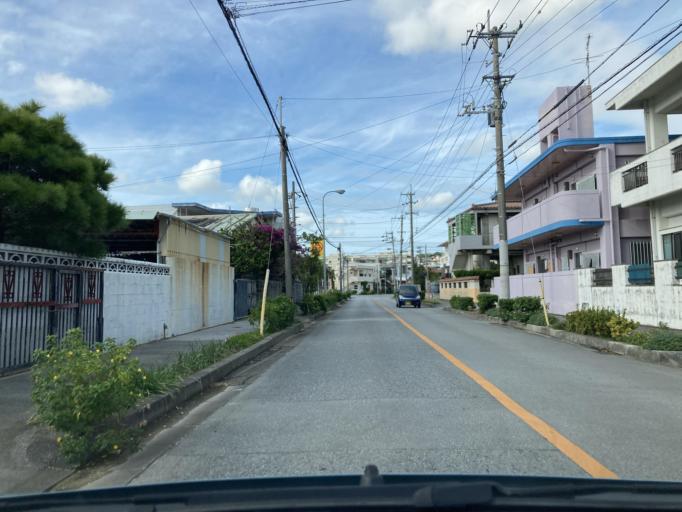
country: JP
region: Okinawa
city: Itoman
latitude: 26.1254
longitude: 127.6775
